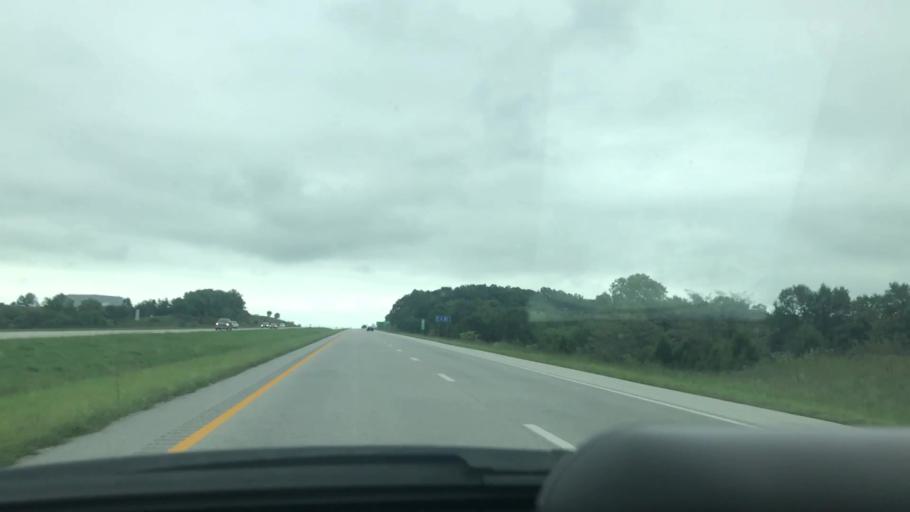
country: US
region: Missouri
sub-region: Greene County
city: Strafford
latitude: 37.2943
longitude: -93.1799
